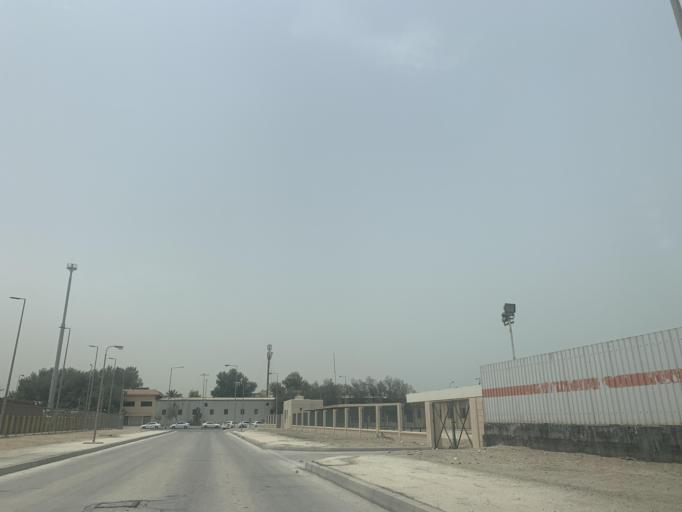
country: BH
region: Northern
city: Sitrah
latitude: 26.1795
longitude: 50.6111
